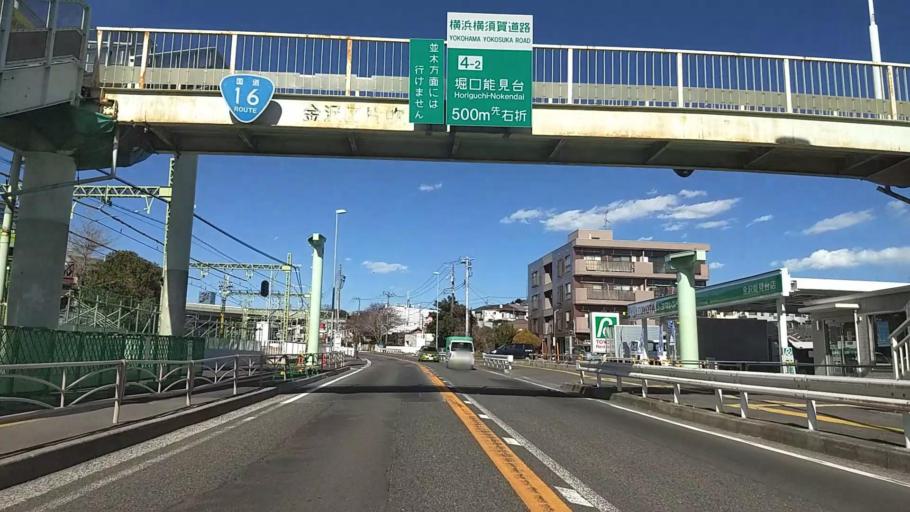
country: JP
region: Kanagawa
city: Zushi
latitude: 35.3531
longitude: 139.6280
